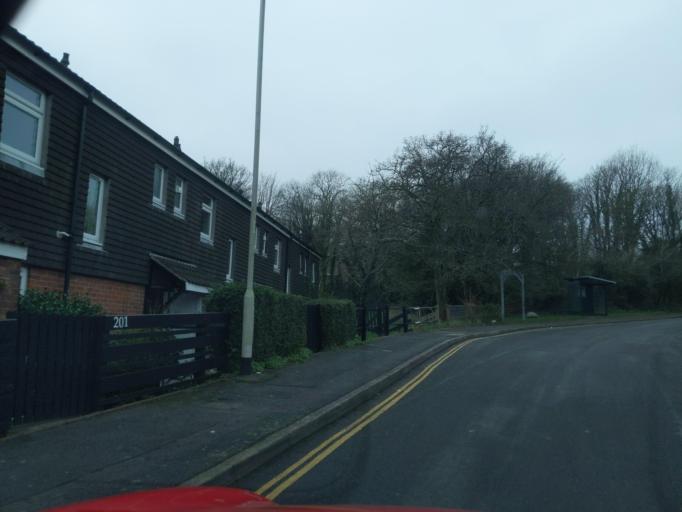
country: GB
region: England
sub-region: Plymouth
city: Plymstock
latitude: 50.3917
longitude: -4.0990
